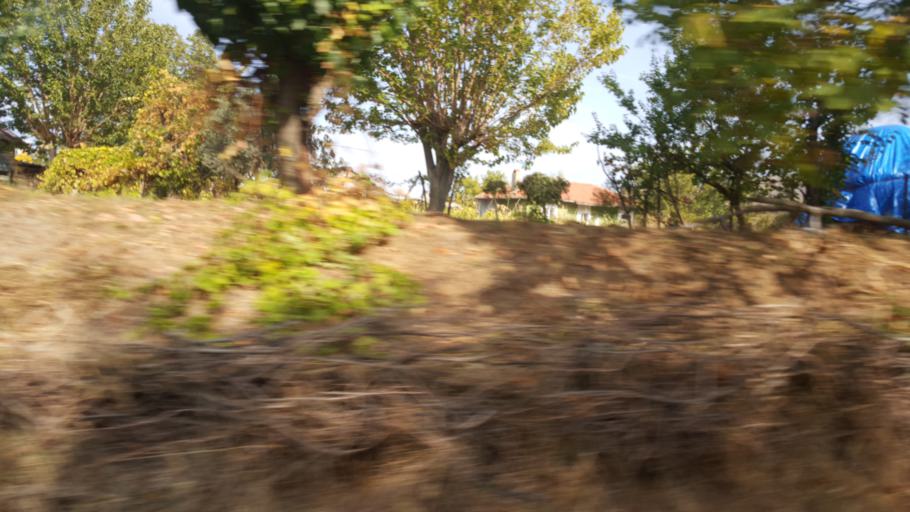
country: TR
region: Eskisehir
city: Mihaliccik
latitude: 39.9769
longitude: 31.3720
